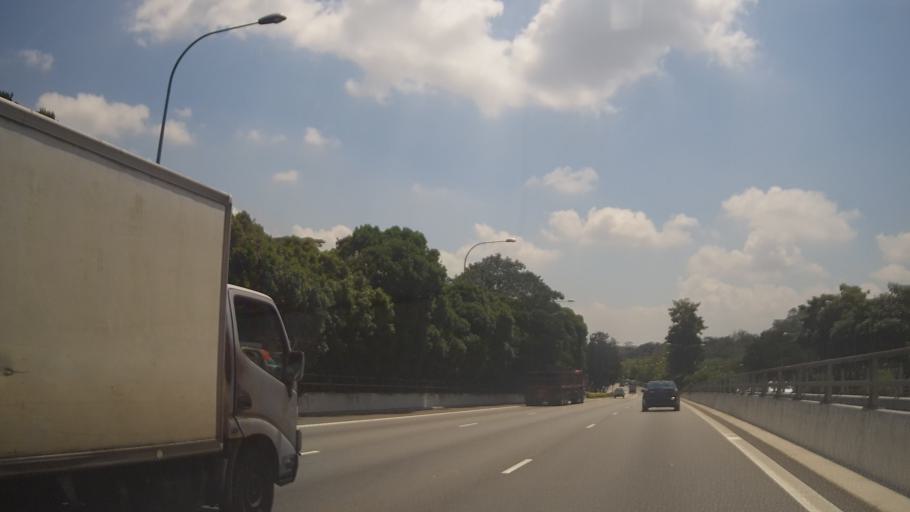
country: MY
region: Johor
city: Johor Bahru
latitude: 1.3942
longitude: 103.8196
